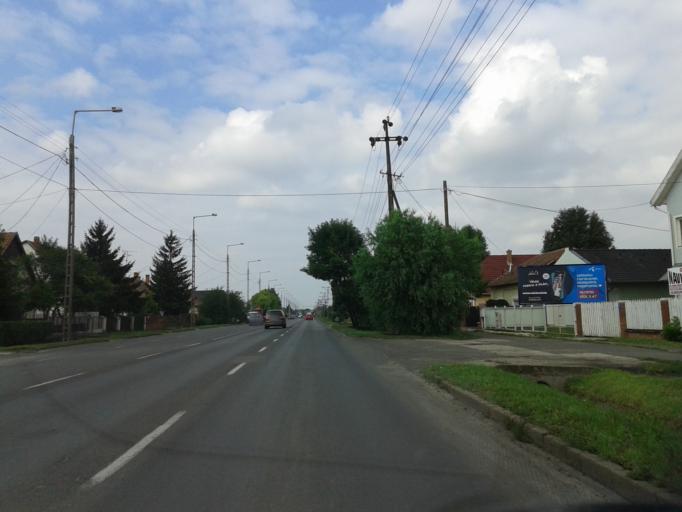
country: HU
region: Csongrad
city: Szeged
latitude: 46.2706
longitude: 20.0892
